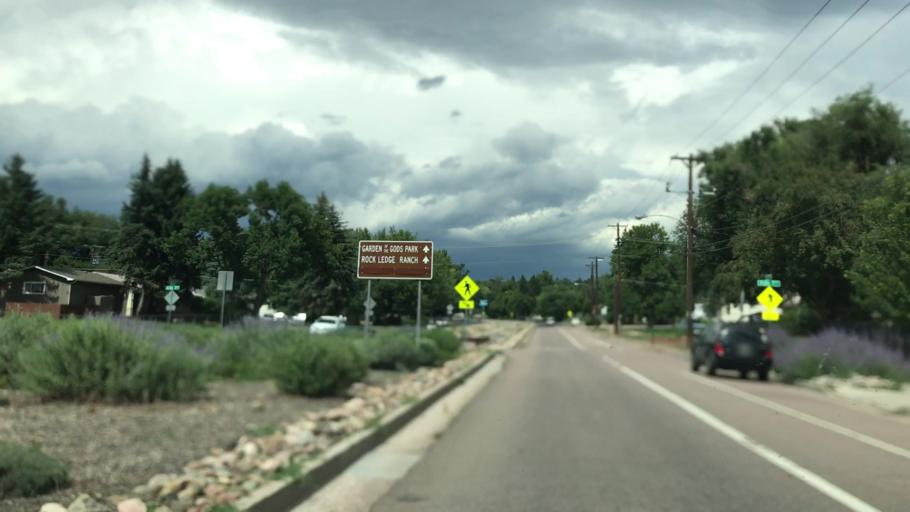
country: US
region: Colorado
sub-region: El Paso County
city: Manitou Springs
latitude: 38.8547
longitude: -104.8705
